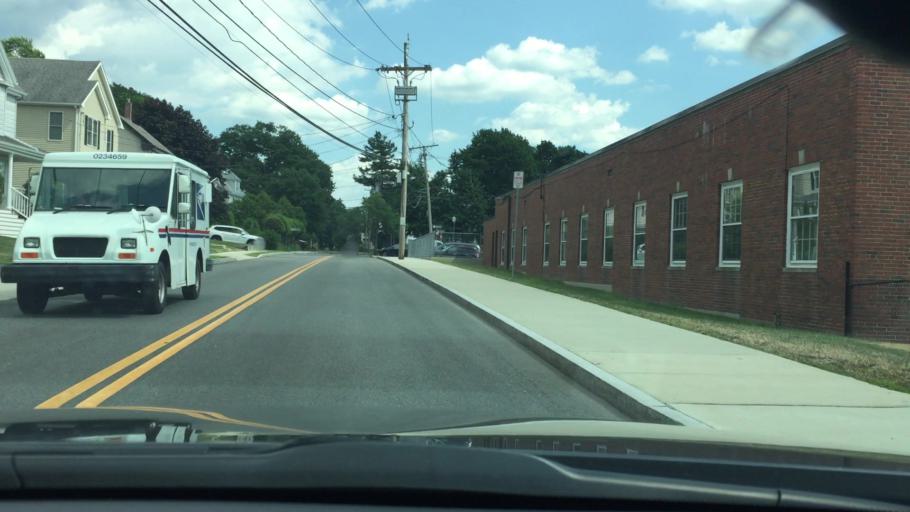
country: US
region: Massachusetts
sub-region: Norfolk County
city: Needham
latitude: 42.2946
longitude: -71.2351
